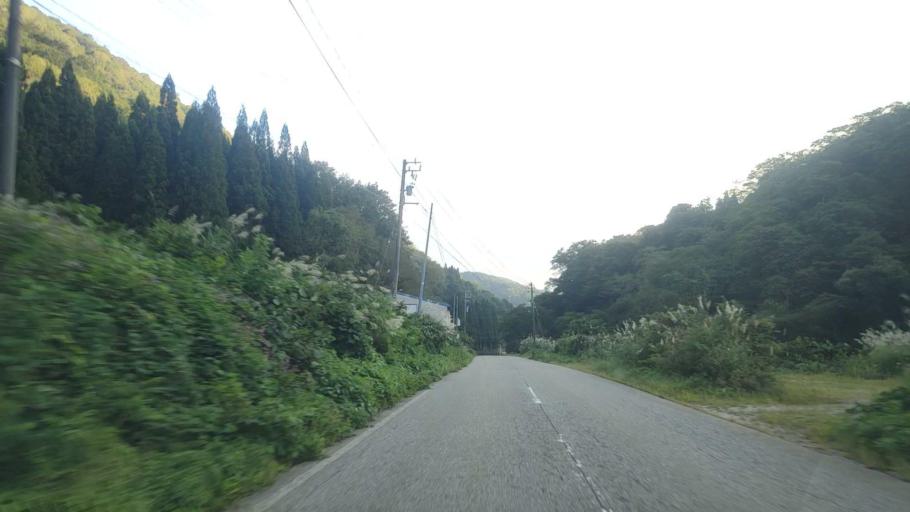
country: JP
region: Toyama
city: Yatsuomachi-higashikumisaka
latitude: 36.4770
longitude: 137.0493
